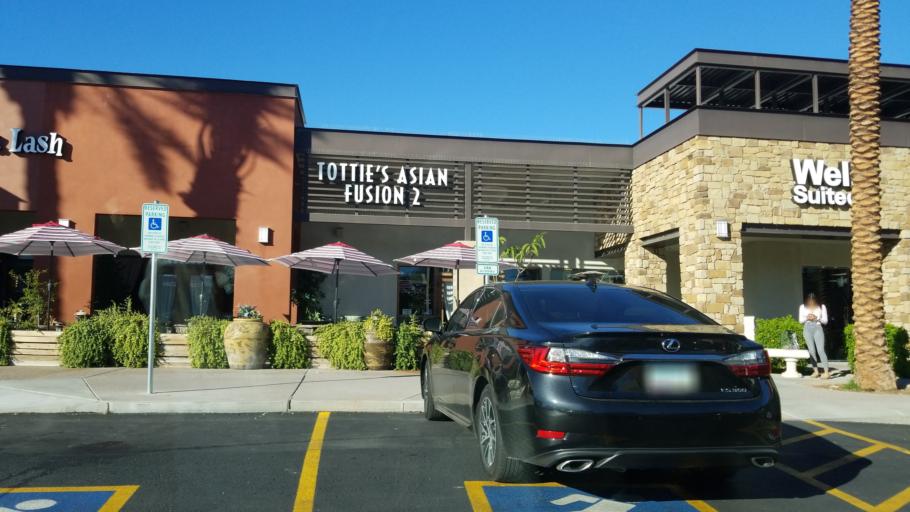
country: US
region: Arizona
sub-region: Maricopa County
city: Paradise Valley
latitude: 33.5294
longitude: -111.9273
